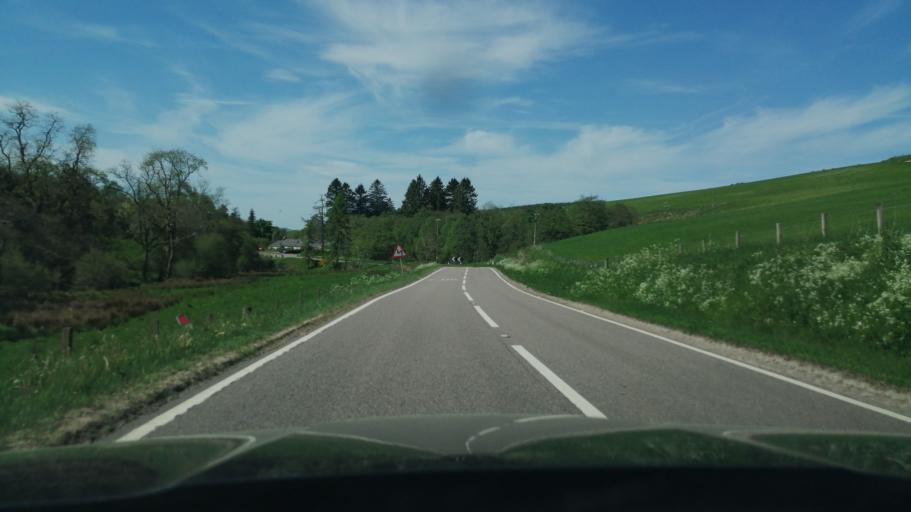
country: GB
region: Scotland
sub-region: Moray
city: Dufftown
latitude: 57.5053
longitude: -3.1265
